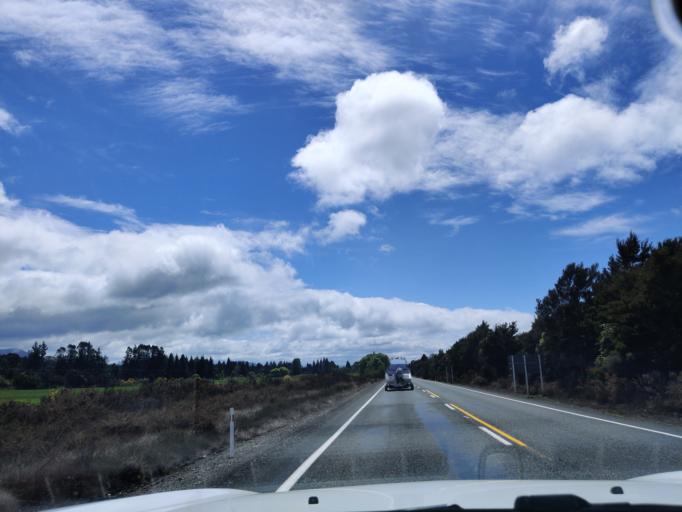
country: NZ
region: Waikato
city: Turangi
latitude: -39.0160
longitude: 175.8080
